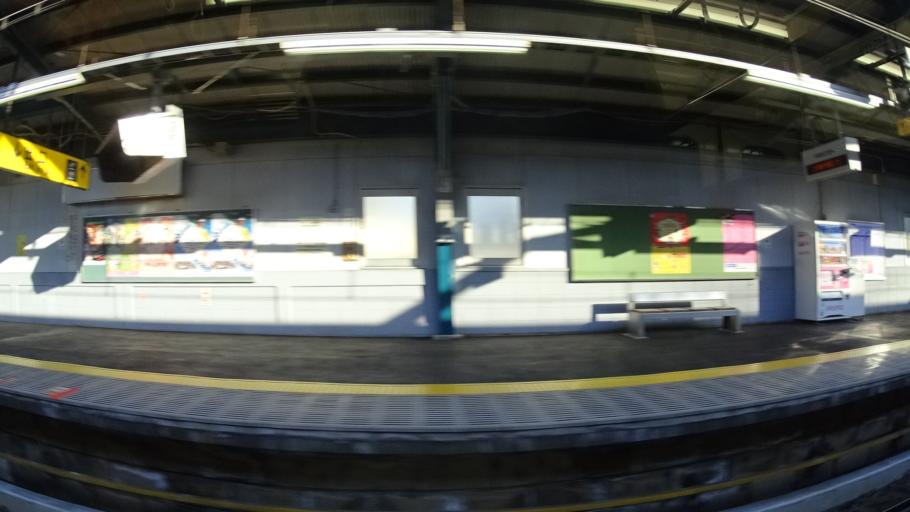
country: JP
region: Kanagawa
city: Miura
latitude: 35.1984
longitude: 139.6653
